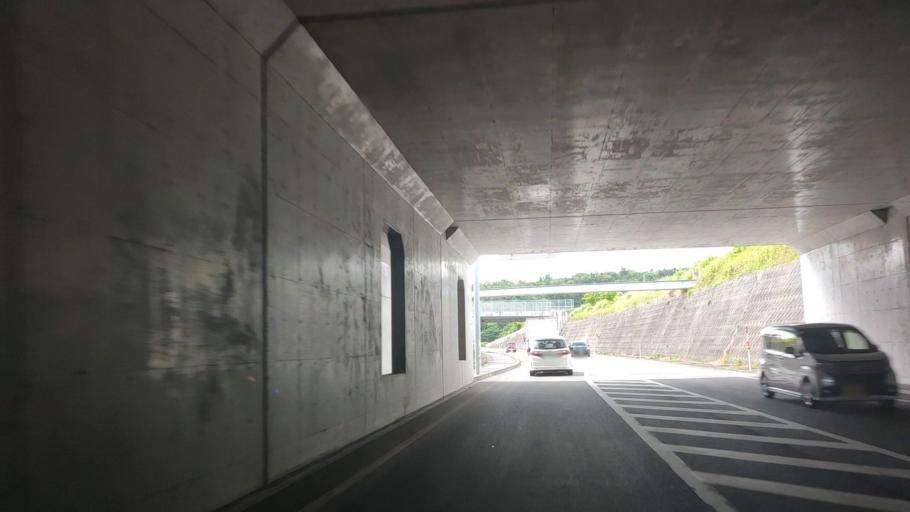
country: JP
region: Tottori
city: Yonago
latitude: 35.3824
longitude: 133.3875
